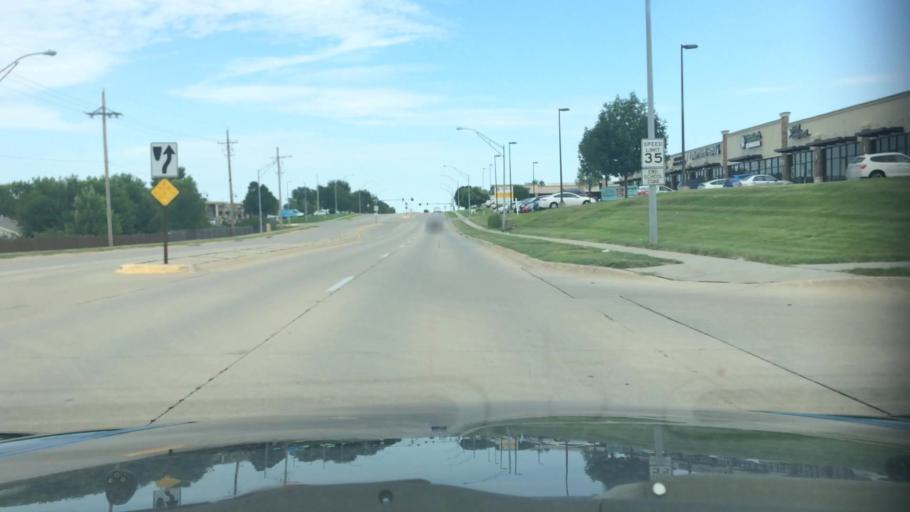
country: US
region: Nebraska
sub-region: Sarpy County
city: La Vista
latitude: 41.1762
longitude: -96.0303
